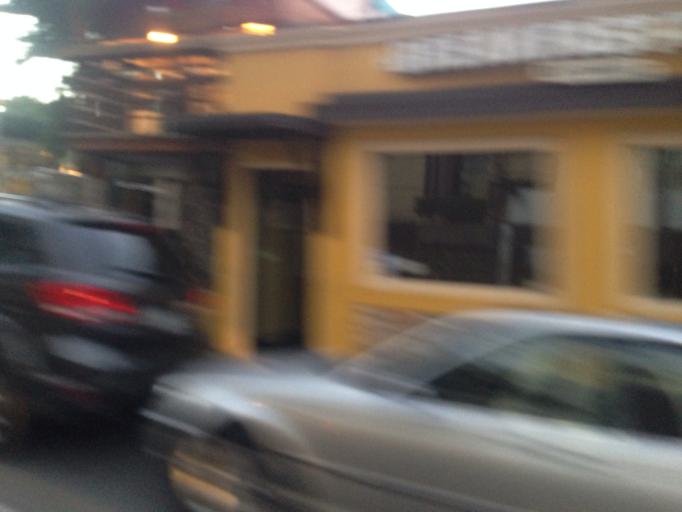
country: MX
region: Baja California
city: Tijuana
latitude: 32.5122
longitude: -117.0128
